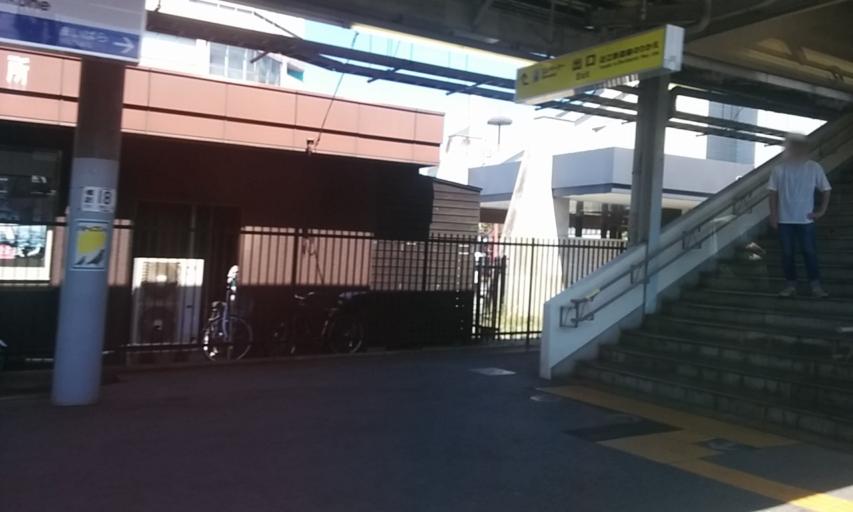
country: JP
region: Shiga Prefecture
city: Hikone
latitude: 35.2719
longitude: 136.2632
